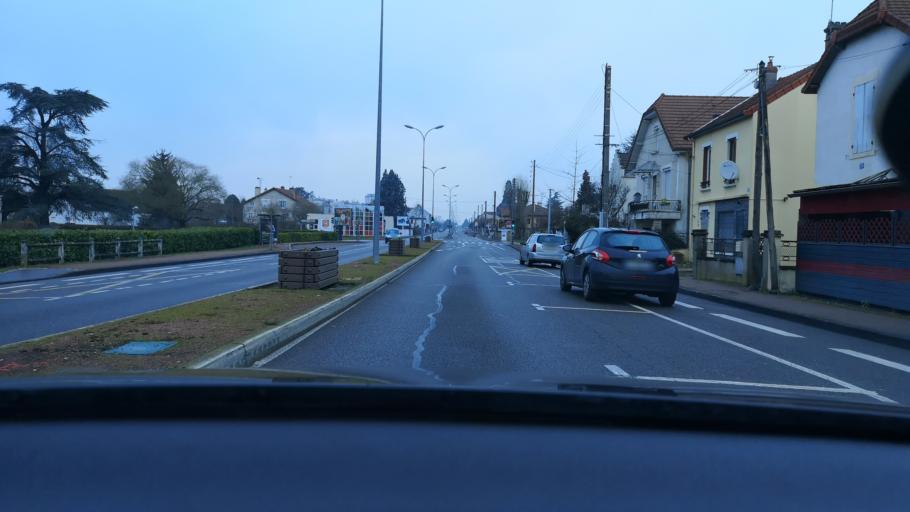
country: FR
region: Bourgogne
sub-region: Departement de Saone-et-Loire
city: Chalon-sur-Saone
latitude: 46.8007
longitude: 4.8464
